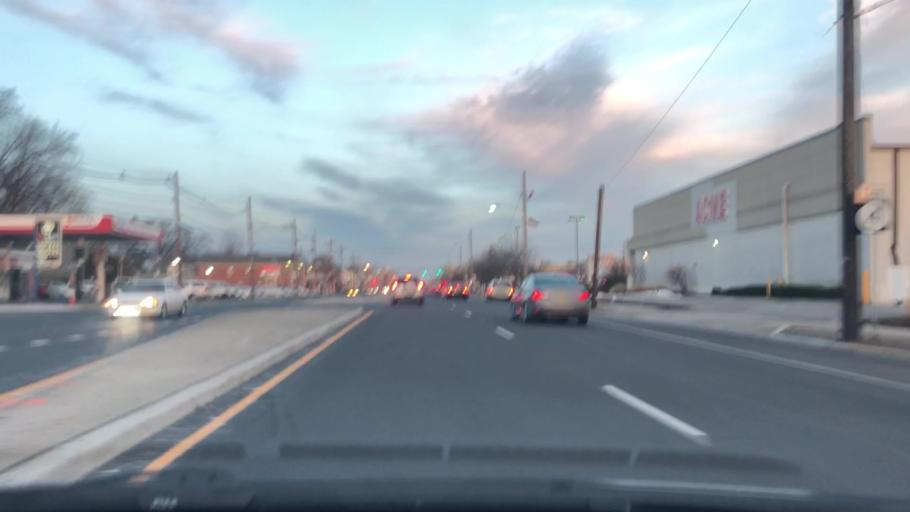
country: US
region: New Jersey
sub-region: Bergen County
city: Elmwood Park
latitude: 40.9184
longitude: -74.1278
